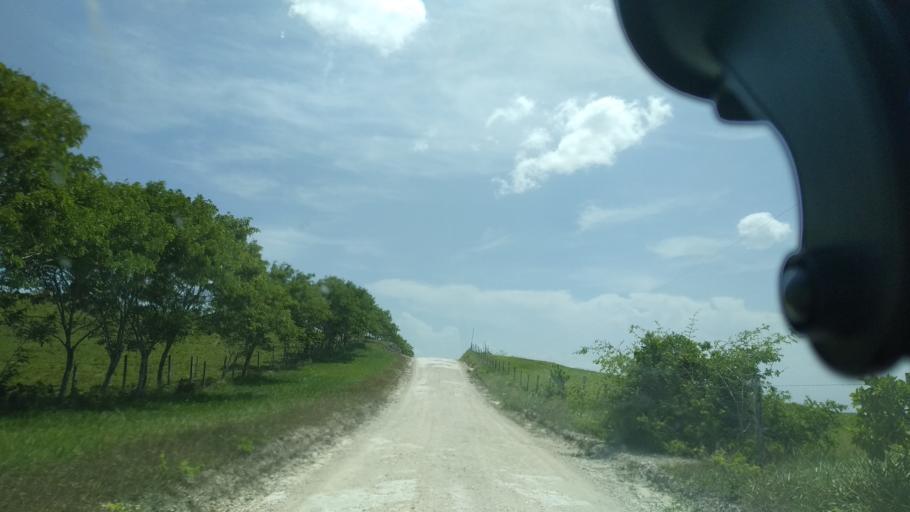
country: BZ
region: Cayo
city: San Ignacio
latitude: 17.2981
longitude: -89.0601
